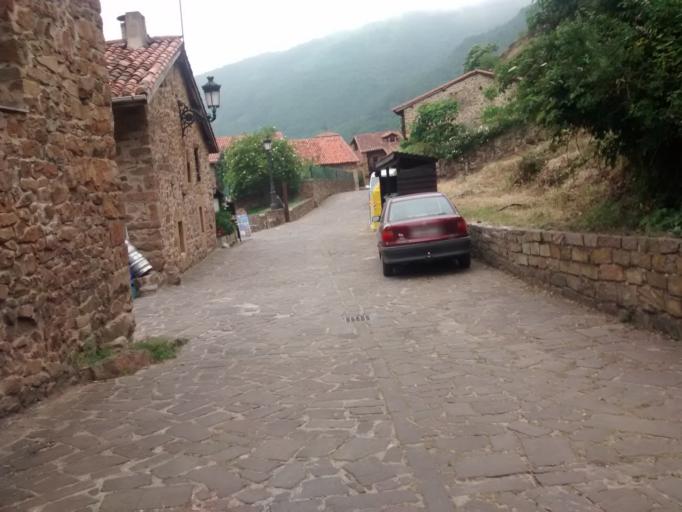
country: ES
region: Cantabria
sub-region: Provincia de Cantabria
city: Pesquera
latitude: 43.1425
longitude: -4.1922
